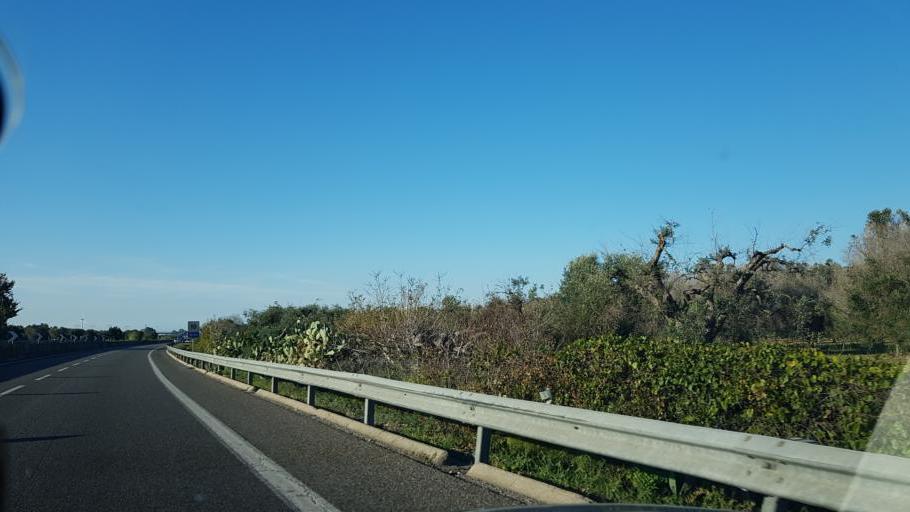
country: IT
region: Apulia
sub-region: Provincia di Brindisi
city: San Pietro Vernotico
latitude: 40.5411
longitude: 18.0024
